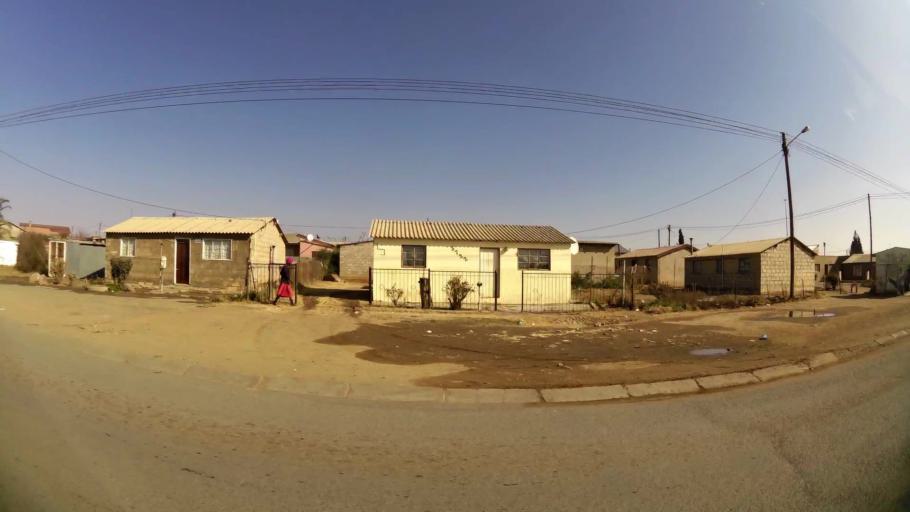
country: ZA
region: Orange Free State
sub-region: Mangaung Metropolitan Municipality
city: Bloemfontein
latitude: -29.1956
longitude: 26.2474
